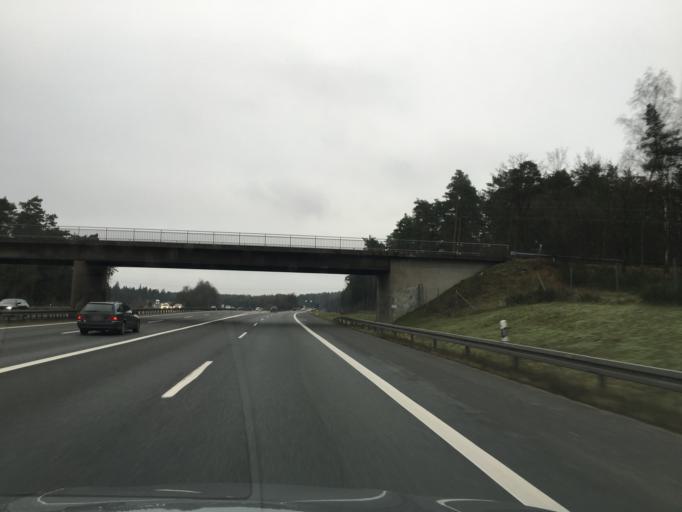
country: DE
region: Bavaria
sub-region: Regierungsbezirk Mittelfranken
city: Rothenbach an der Pegnitz
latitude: 49.4473
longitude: 11.2335
